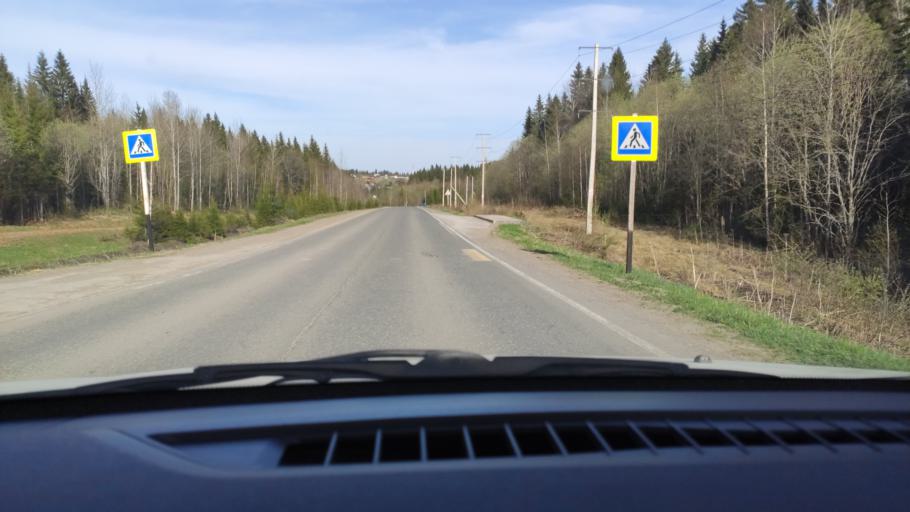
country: RU
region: Perm
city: Novyye Lyady
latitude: 57.9413
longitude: 56.6180
